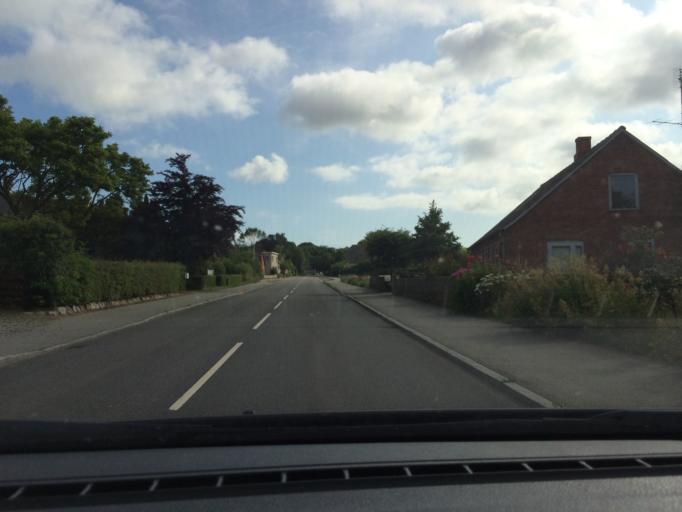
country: DK
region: Zealand
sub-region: Vordingborg Kommune
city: Stege
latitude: 54.9940
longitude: 12.3850
